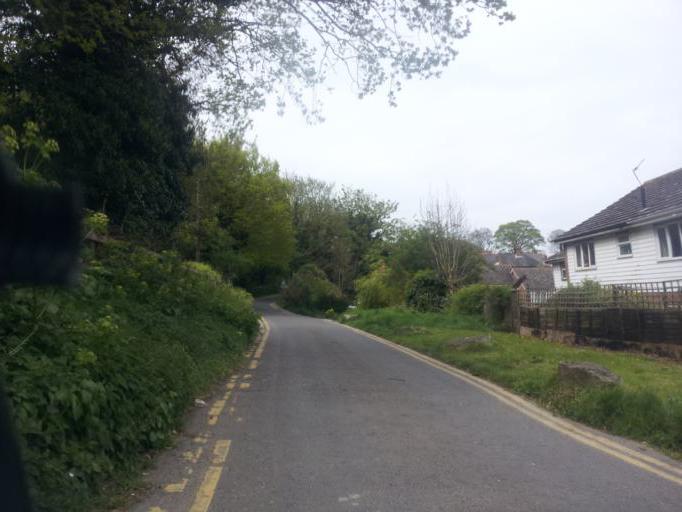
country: GB
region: England
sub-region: Medway
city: Rochester
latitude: 51.4052
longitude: 0.5247
